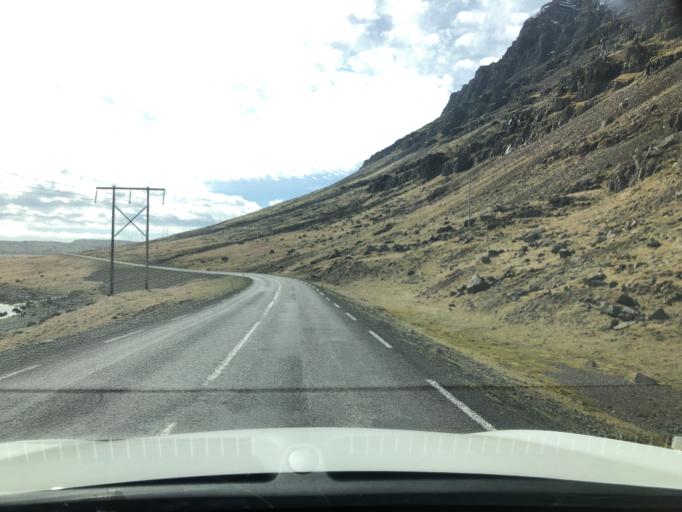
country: IS
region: East
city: Reydarfjoerdur
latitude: 64.7067
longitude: -14.3961
